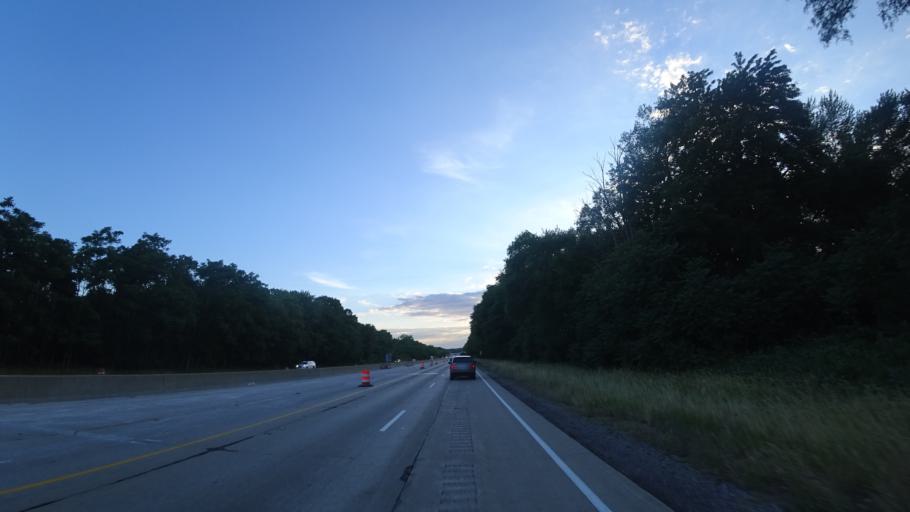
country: US
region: Indiana
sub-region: LaPorte County
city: Trail Creek
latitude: 41.6763
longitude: -86.8353
